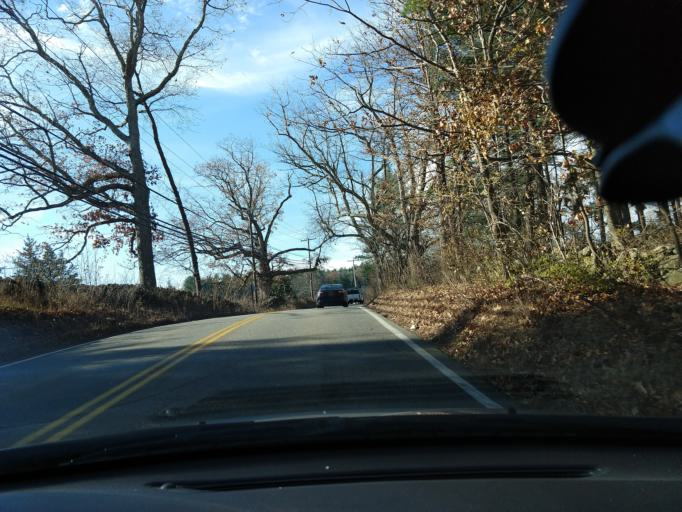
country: US
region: Massachusetts
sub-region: Middlesex County
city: Dunstable
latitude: 42.6823
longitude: -71.4577
